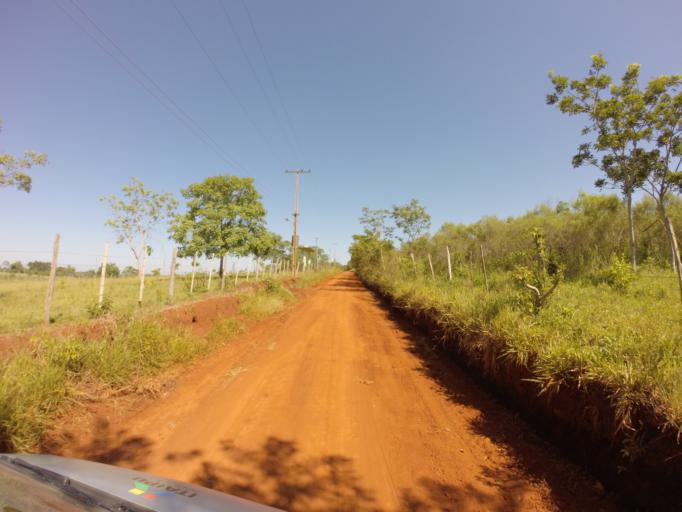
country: PY
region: Alto Parana
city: Ciudad del Este
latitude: -25.4414
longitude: -54.6622
